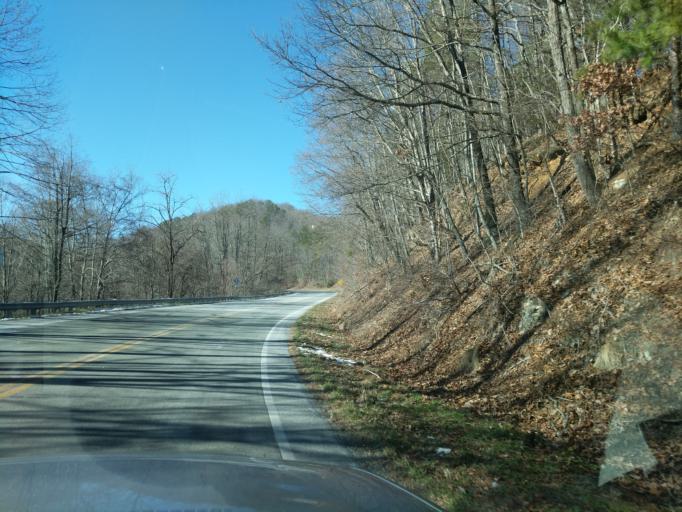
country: US
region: Georgia
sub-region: Towns County
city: Hiawassee
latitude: 34.8919
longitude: -83.5870
